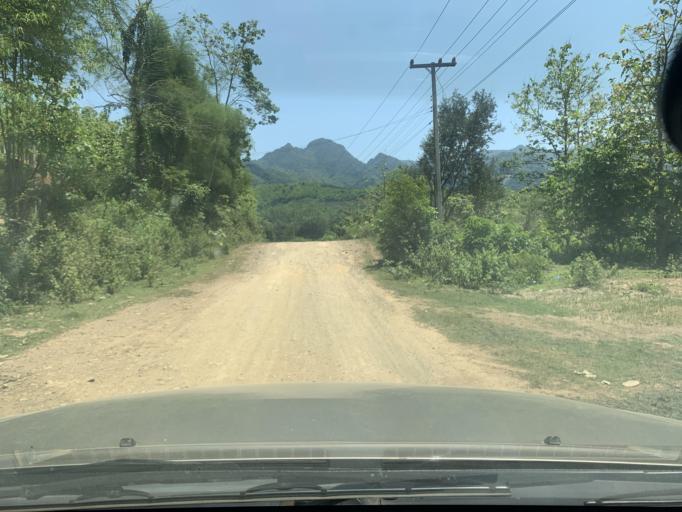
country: LA
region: Louangphabang
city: Louangphabang
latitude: 19.9039
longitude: 102.2522
